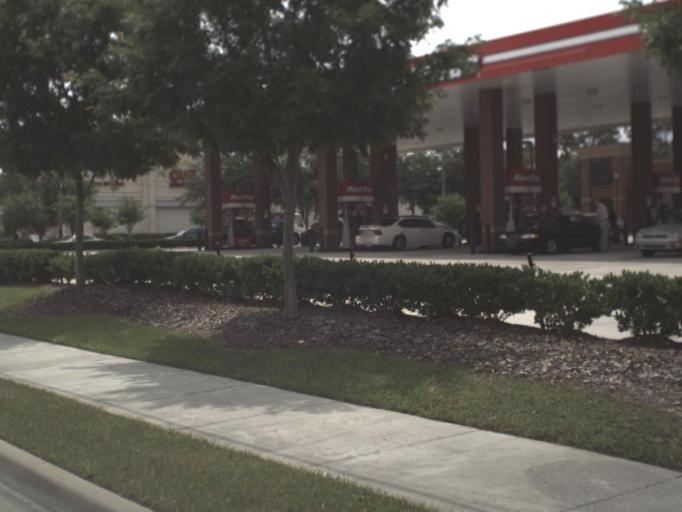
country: US
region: Florida
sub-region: Duval County
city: Jacksonville
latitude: 30.4298
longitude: -81.6663
